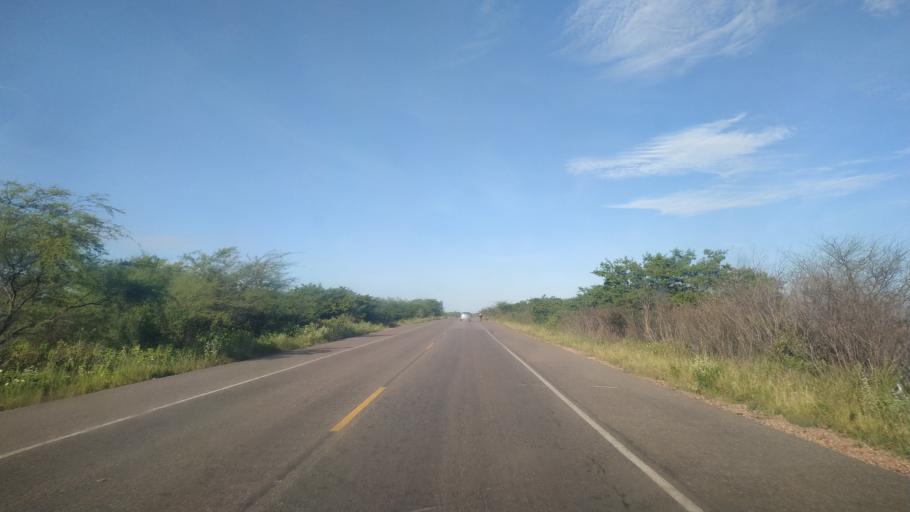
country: BR
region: Rio Grande do Norte
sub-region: Areia Branca
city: Areia Branca
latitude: -5.0447
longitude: -37.1419
